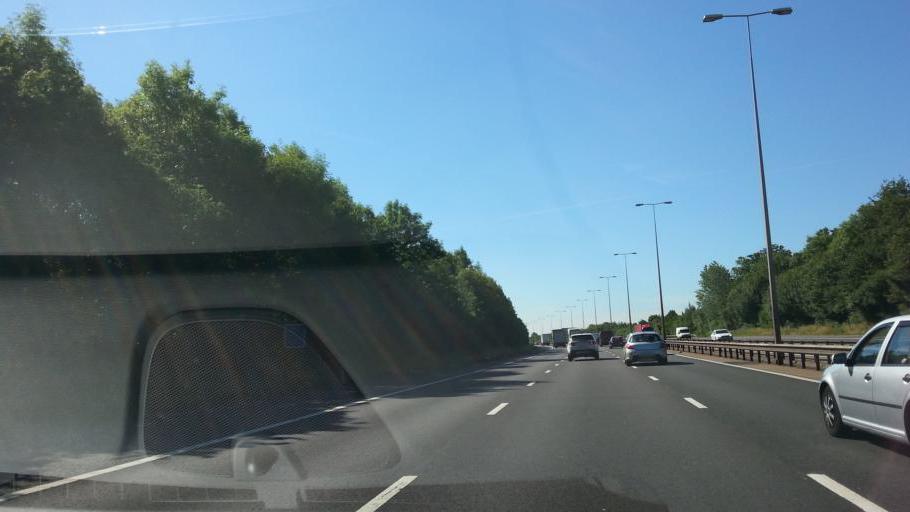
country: GB
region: England
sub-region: Worcestershire
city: Upton upon Severn
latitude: 52.0983
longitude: -2.1861
